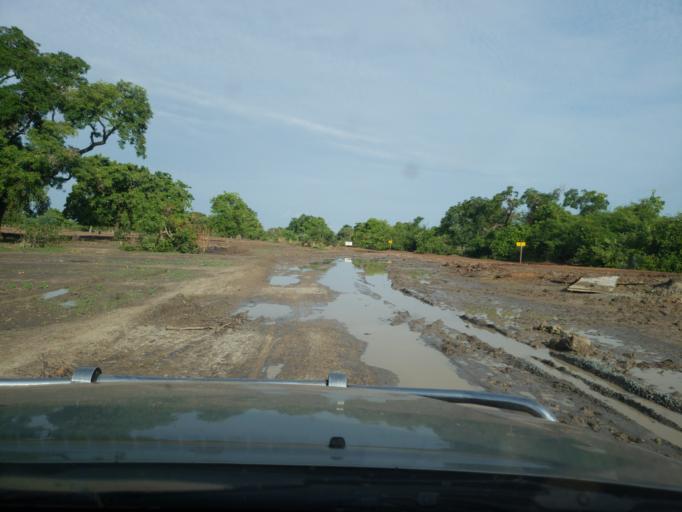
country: ML
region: Sikasso
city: Koutiala
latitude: 12.4186
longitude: -5.7041
